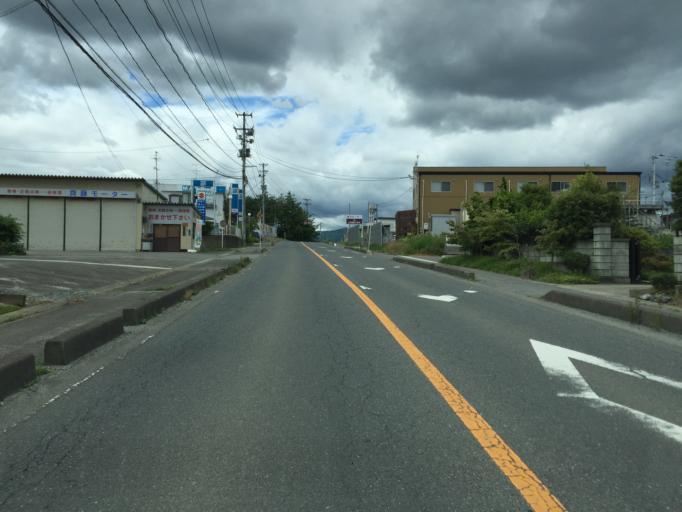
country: JP
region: Fukushima
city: Namie
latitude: 37.6217
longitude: 140.9813
